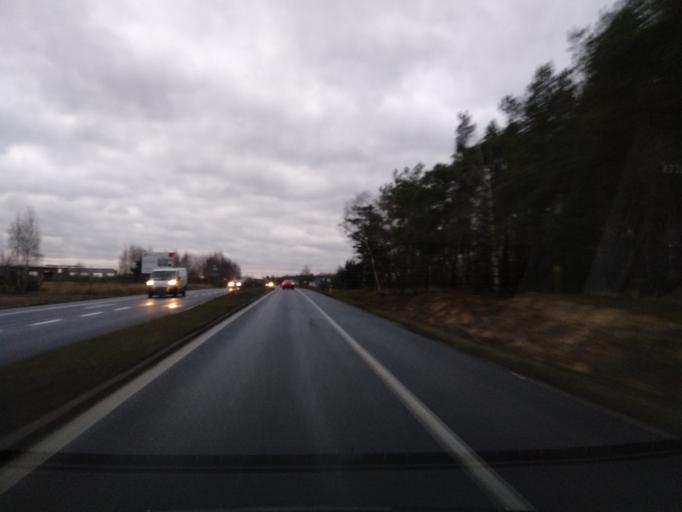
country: PL
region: Greater Poland Voivodeship
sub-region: Powiat koninski
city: Stare Miasto
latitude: 52.1698
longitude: 18.2126
